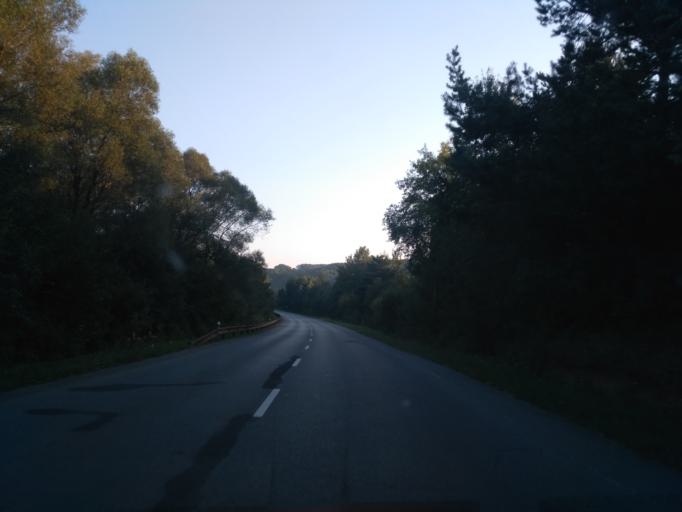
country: SK
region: Presovsky
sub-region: Okres Presov
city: Presov
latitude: 48.9595
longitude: 21.1633
